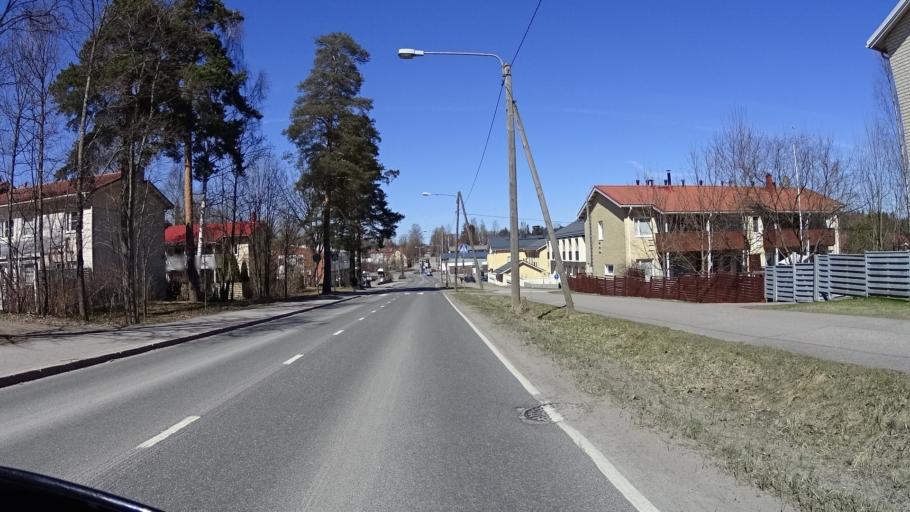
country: FI
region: Uusimaa
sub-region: Helsinki
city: Kilo
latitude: 60.2323
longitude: 24.8137
